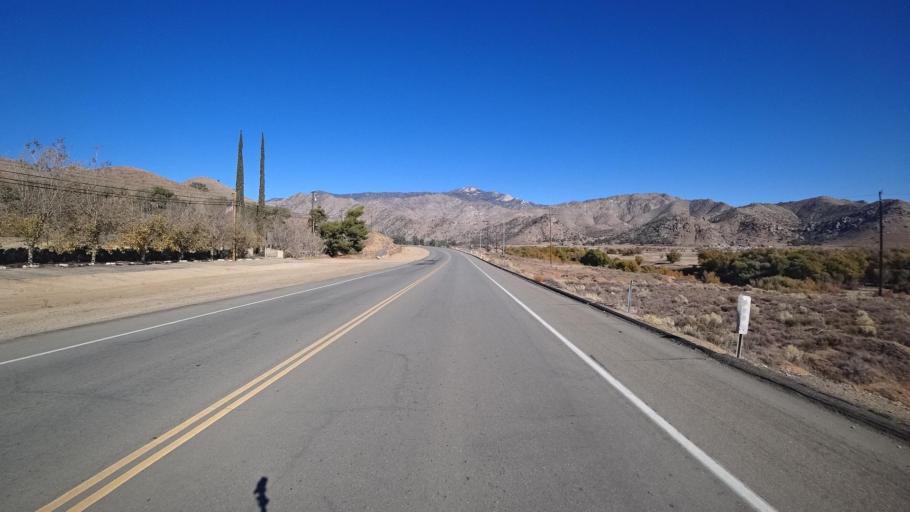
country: US
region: California
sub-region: Kern County
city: Wofford Heights
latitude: 35.7211
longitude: -118.4353
